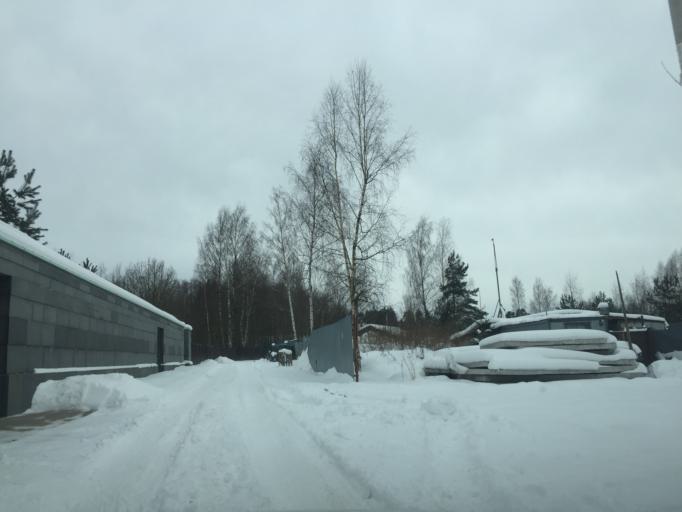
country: RU
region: Leningrad
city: Otradnoye
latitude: 59.7825
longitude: 30.7877
